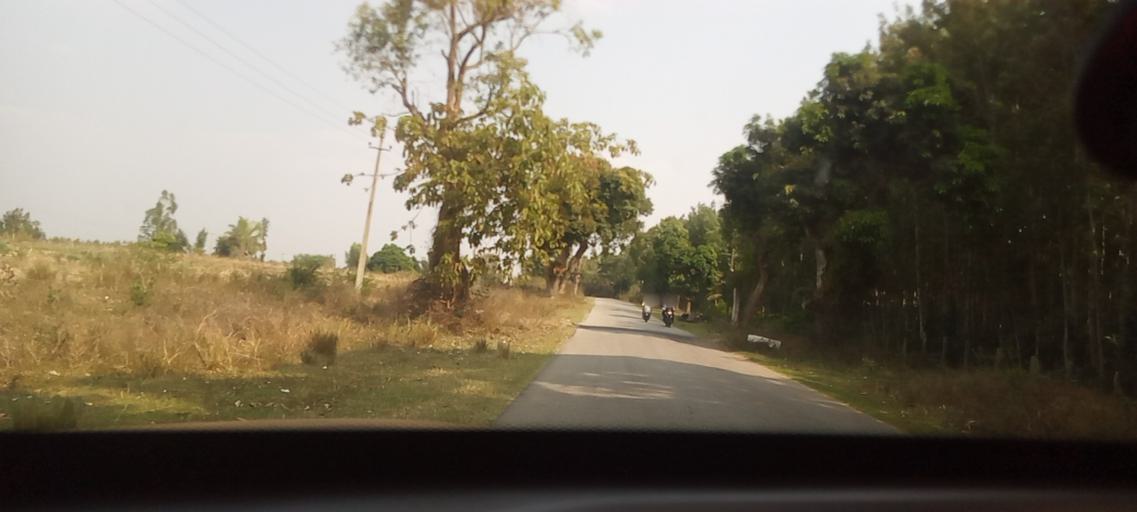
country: IN
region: Karnataka
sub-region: Hassan
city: Belur
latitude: 13.1828
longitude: 75.8382
